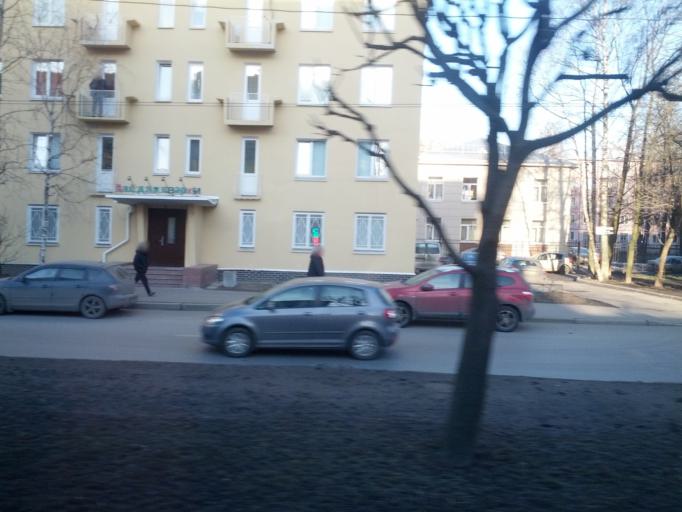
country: RU
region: St.-Petersburg
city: Centralniy
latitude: 59.9209
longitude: 30.4216
